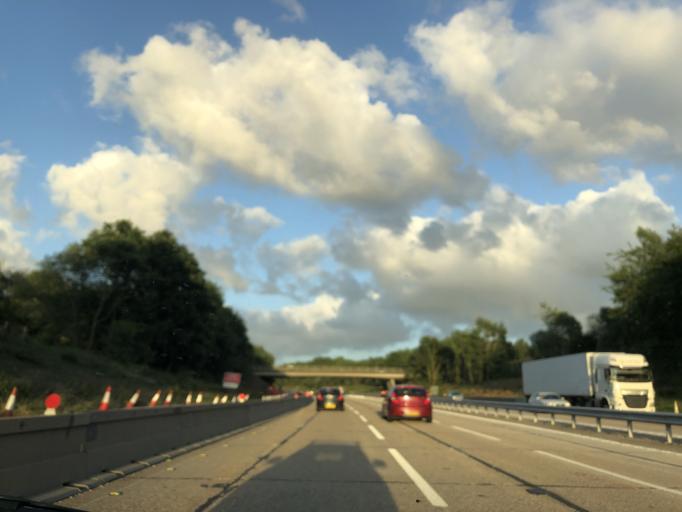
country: GB
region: England
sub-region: Hampshire
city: West End
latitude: 50.9373
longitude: -1.3510
